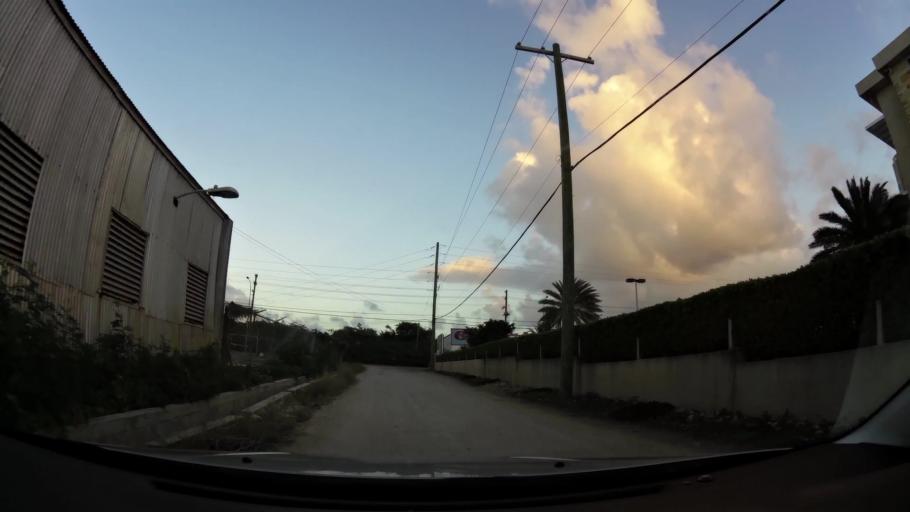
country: AG
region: Saint John
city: Saint John's
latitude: 17.1356
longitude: -61.8366
